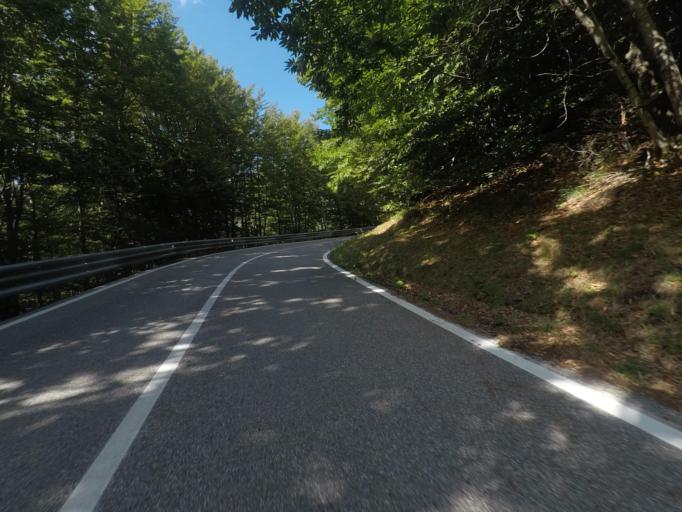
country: IT
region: Tuscany
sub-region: Provincia di Massa-Carrara
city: Comano
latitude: 44.2892
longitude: 10.2054
